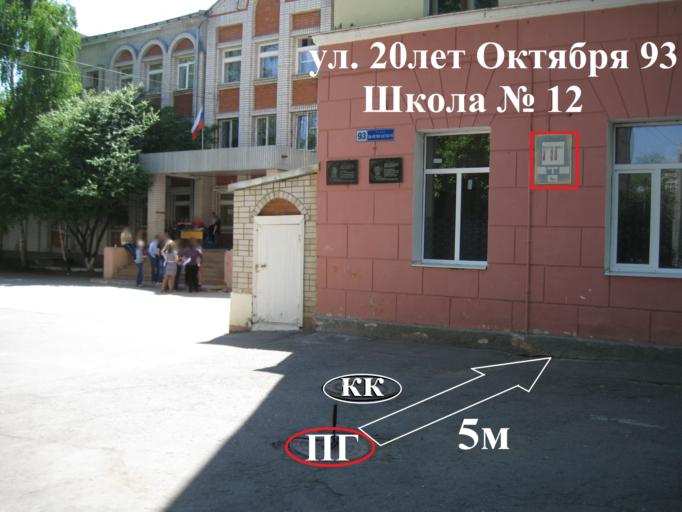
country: RU
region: Voronezj
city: Voronezh
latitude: 51.6503
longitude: 39.1921
